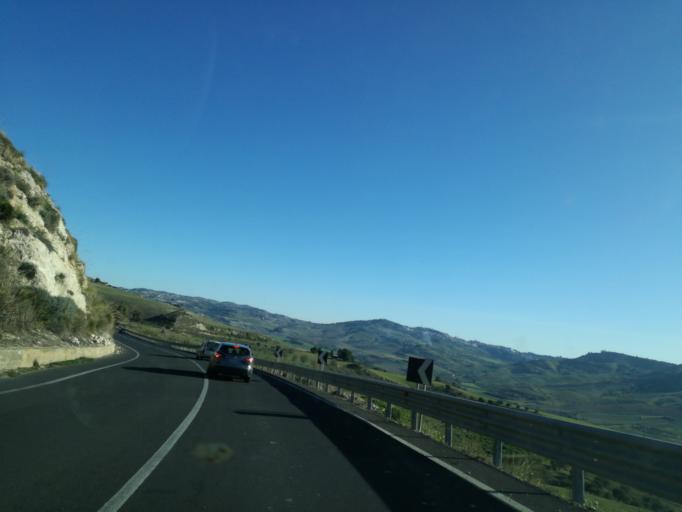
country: IT
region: Sicily
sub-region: Catania
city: San Michele di Ganzaria
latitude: 37.2274
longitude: 14.4373
